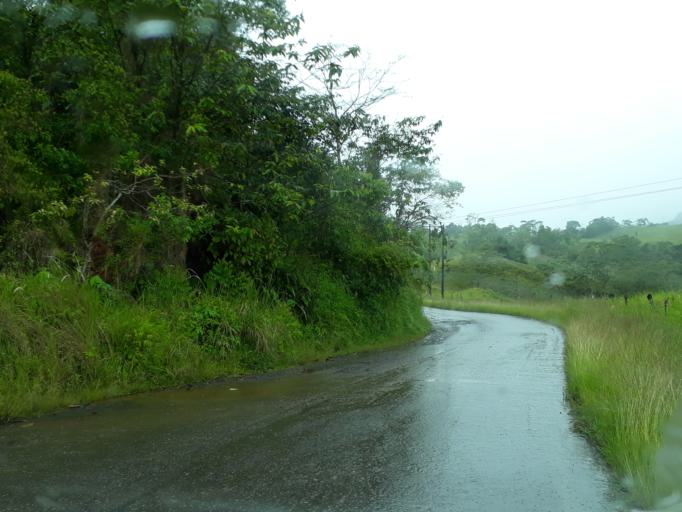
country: CO
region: Cundinamarca
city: Medina
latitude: 4.6587
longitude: -73.3277
